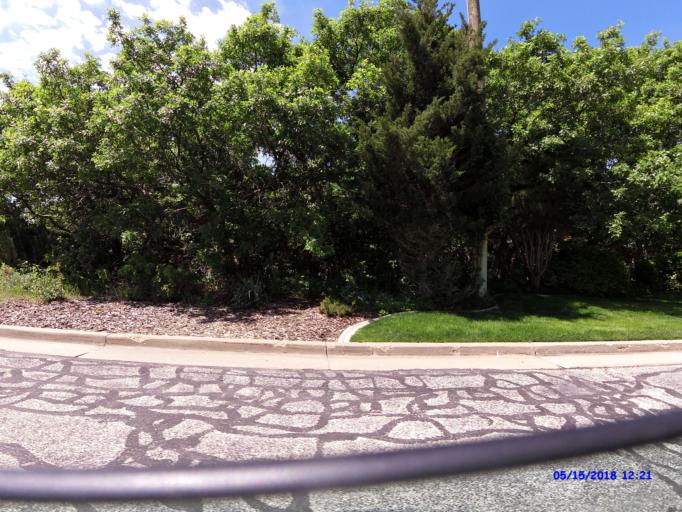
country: US
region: Utah
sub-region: Weber County
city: Uintah
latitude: 41.1666
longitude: -111.9227
